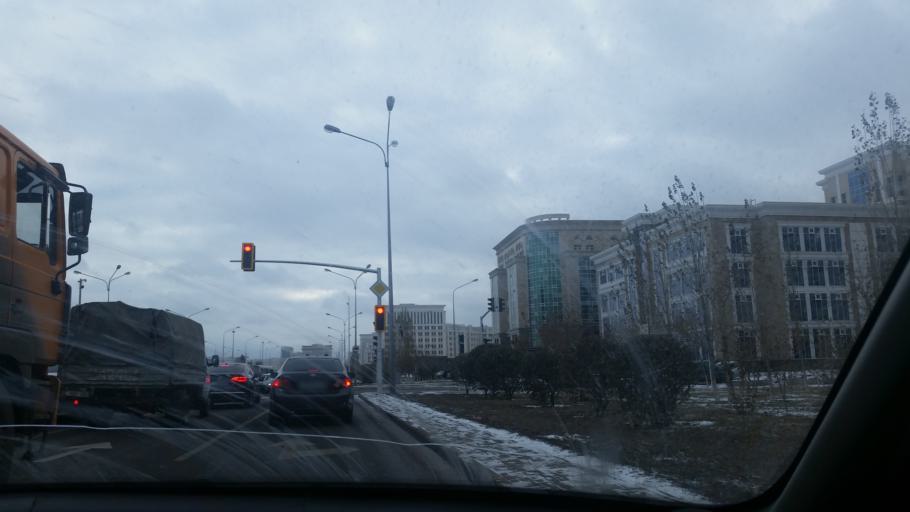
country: KZ
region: Astana Qalasy
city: Astana
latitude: 51.1092
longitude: 71.4316
